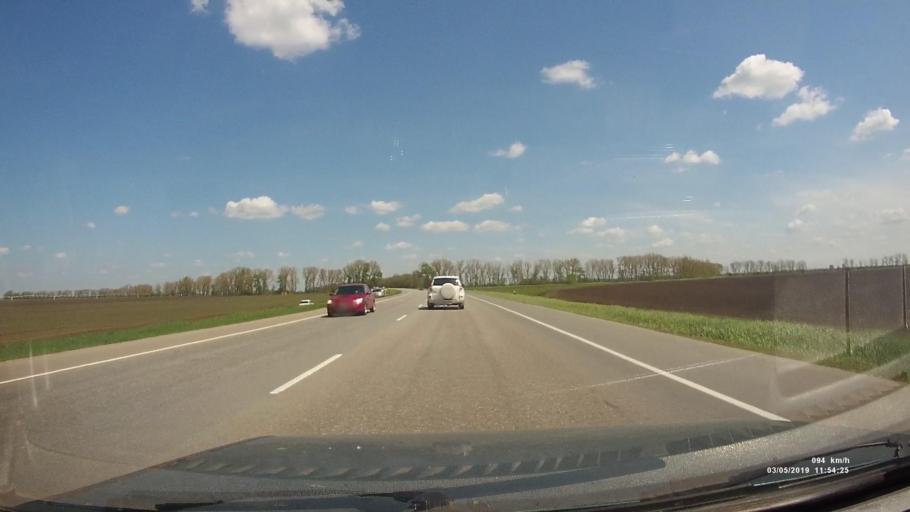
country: RU
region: Rostov
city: Bagayevskaya
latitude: 47.1699
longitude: 40.2798
